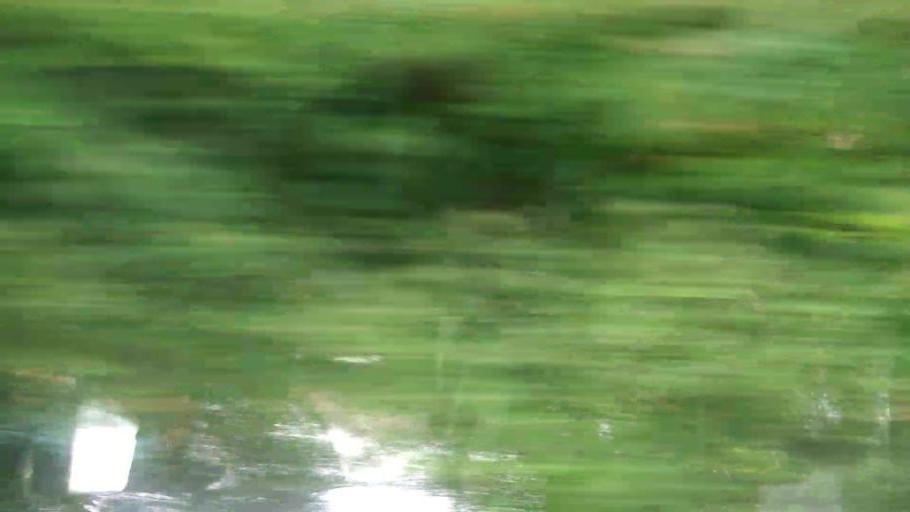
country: RU
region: Moskovskaya
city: Lukhovitsy
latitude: 54.9284
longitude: 39.0023
